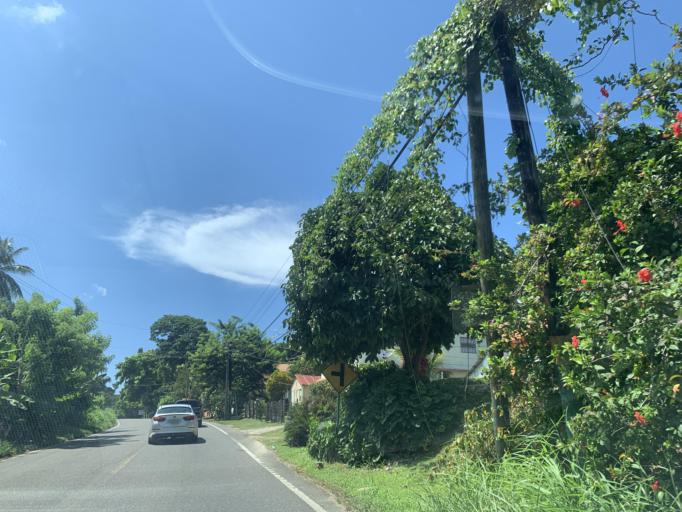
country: DO
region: Maria Trinidad Sanchez
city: Cabrera
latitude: 19.6503
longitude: -69.9303
